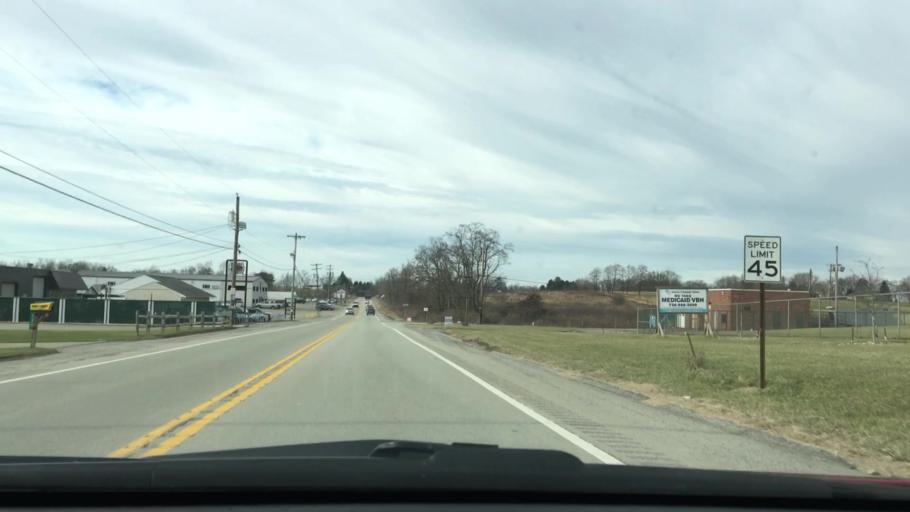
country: US
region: Pennsylvania
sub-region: Fayette County
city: South Uniontown
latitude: 39.8934
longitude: -79.7995
